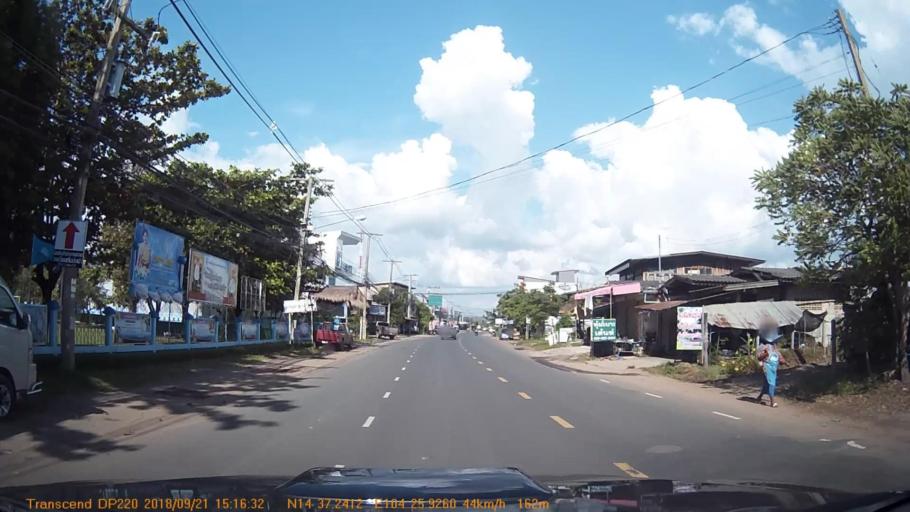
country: TH
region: Sisaket
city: Khun Han
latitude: 14.6208
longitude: 104.4323
